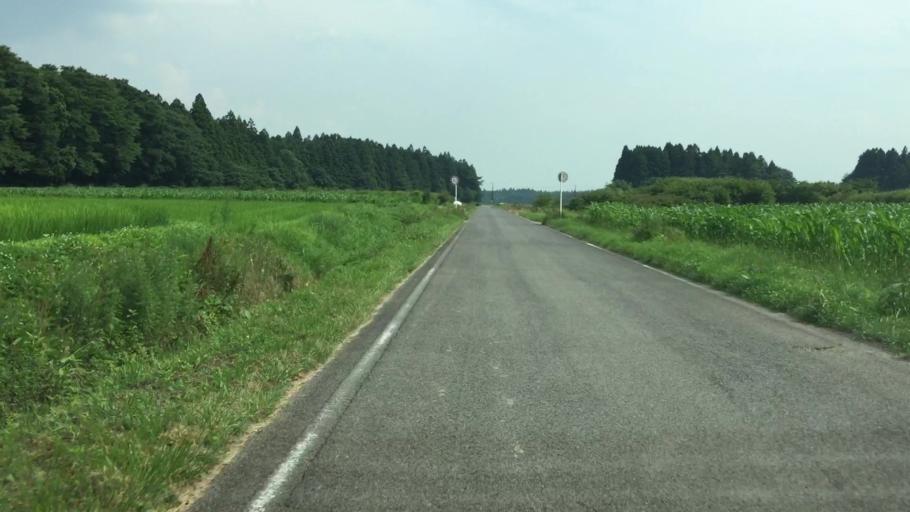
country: JP
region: Tochigi
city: Kuroiso
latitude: 37.0148
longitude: 139.9499
